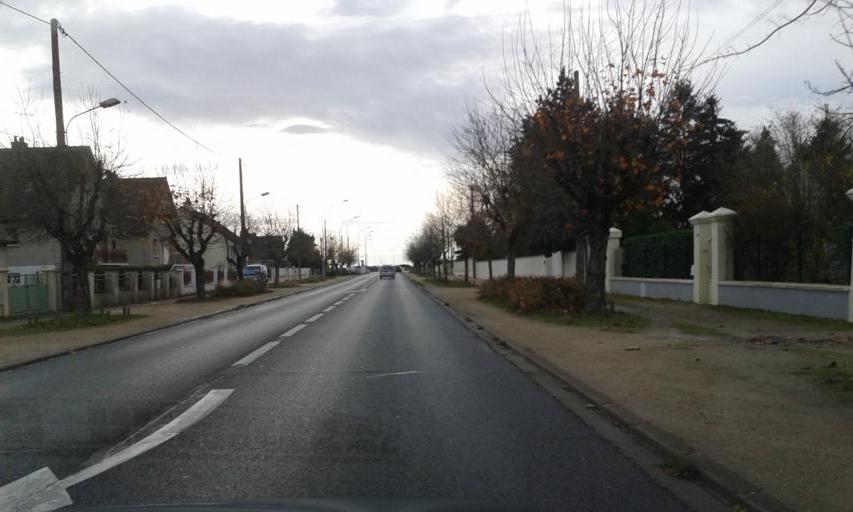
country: FR
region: Centre
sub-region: Departement du Loiret
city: Meung-sur-Loire
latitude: 47.8235
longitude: 1.6870
